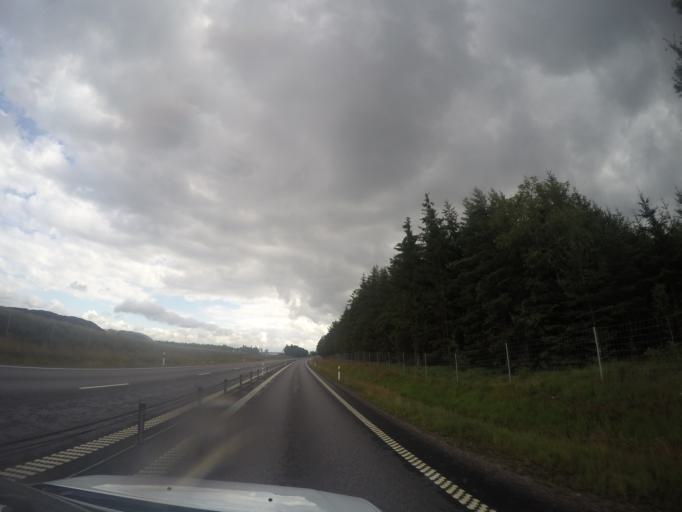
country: SE
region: Kronoberg
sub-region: Ljungby Kommun
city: Ljungby
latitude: 56.8097
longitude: 13.8915
